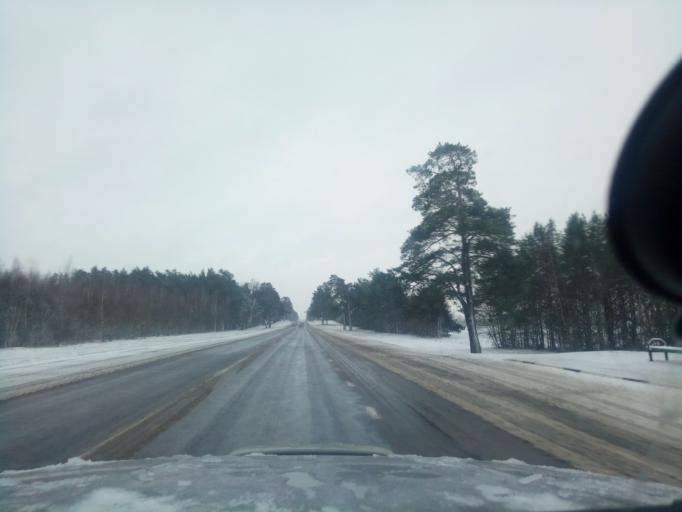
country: BY
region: Minsk
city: Nyasvizh
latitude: 53.2559
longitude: 26.6155
